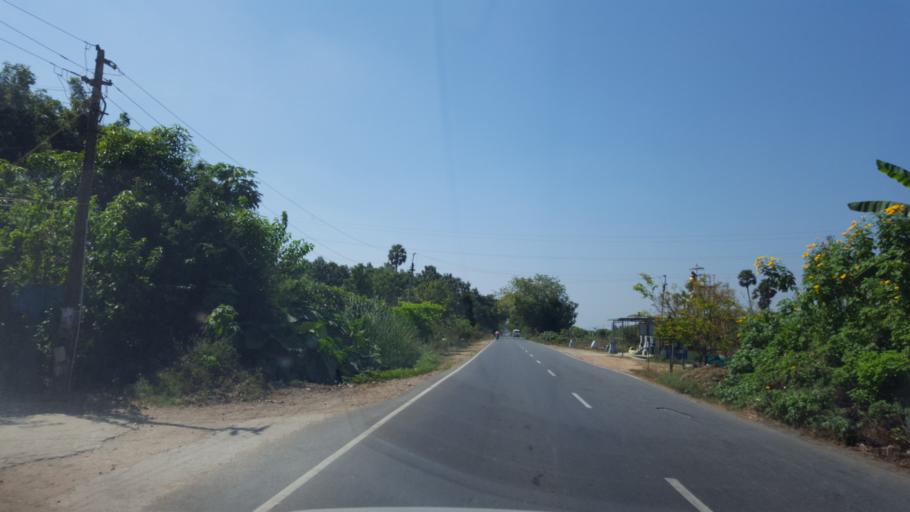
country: IN
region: Tamil Nadu
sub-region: Kancheepuram
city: Chengalpattu
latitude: 12.7554
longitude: 79.9272
